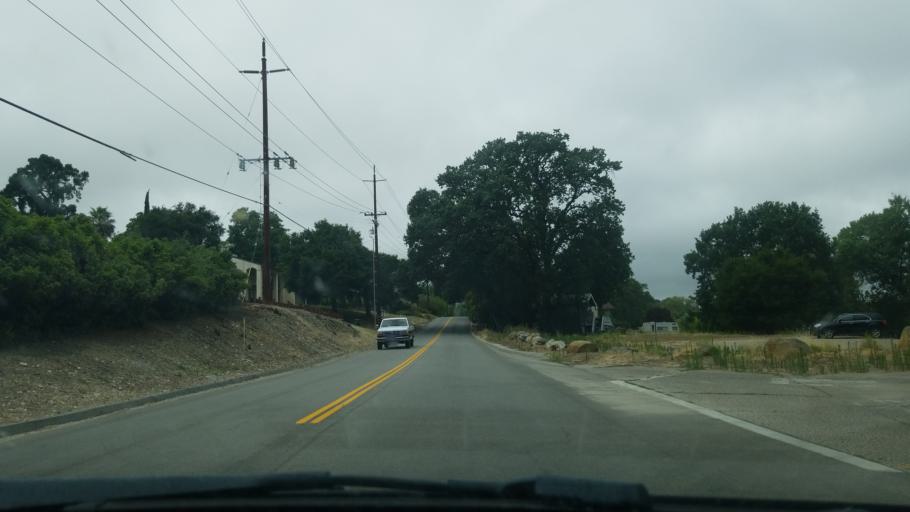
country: US
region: California
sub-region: San Luis Obispo County
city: Atascadero
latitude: 35.4620
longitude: -120.6658
